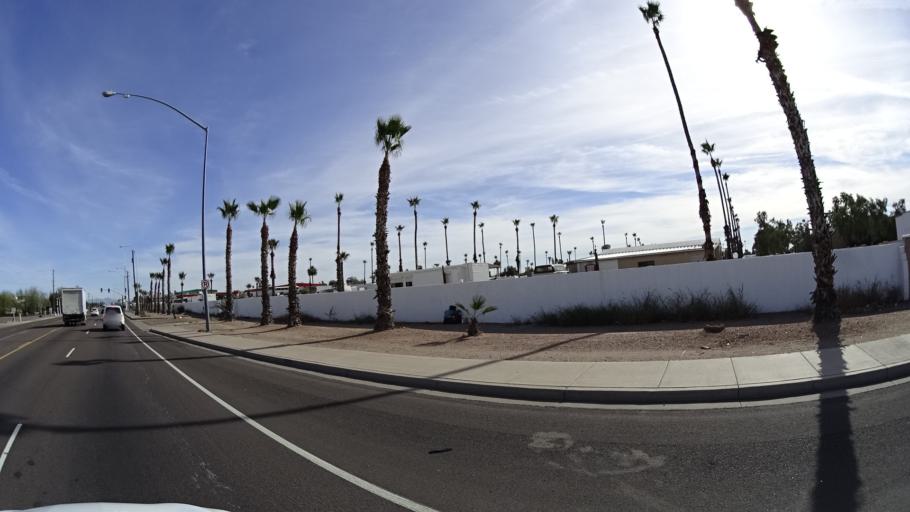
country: US
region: Arizona
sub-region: Maricopa County
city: Tempe
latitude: 33.4075
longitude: -111.8714
